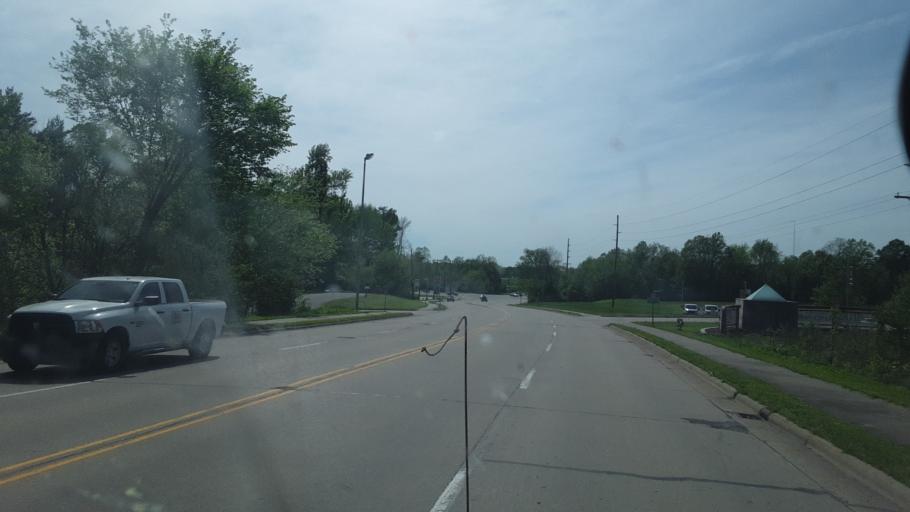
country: US
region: Illinois
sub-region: Jackson County
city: Carbondale
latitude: 37.7005
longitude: -89.2153
